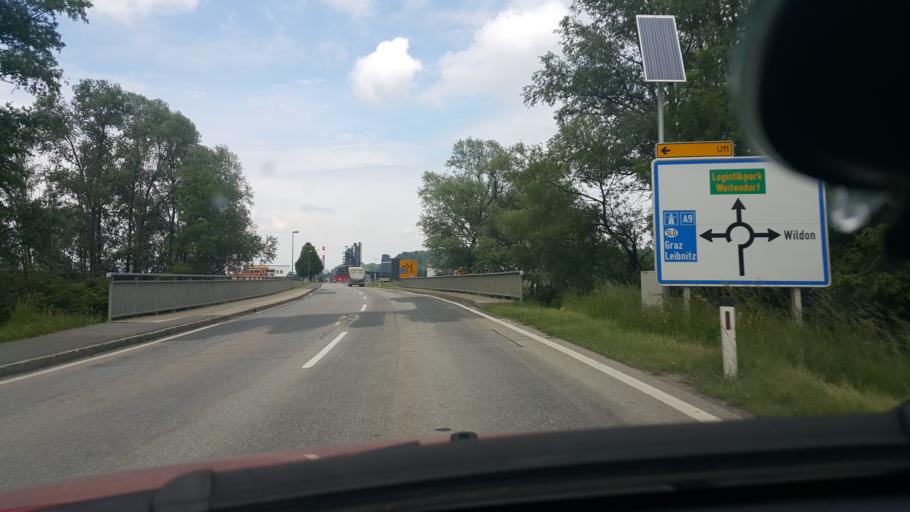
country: AT
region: Styria
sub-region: Politischer Bezirk Leibnitz
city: Weitendorf
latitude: 46.8840
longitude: 15.4890
